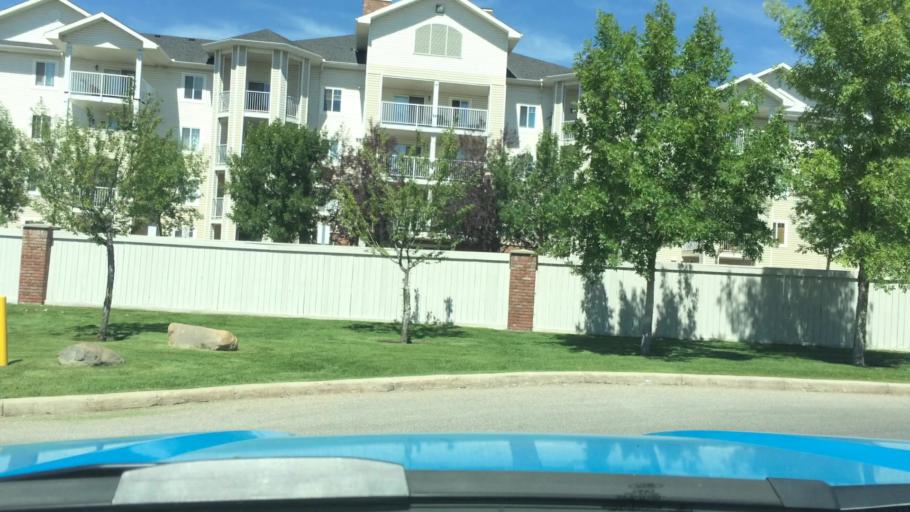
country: CA
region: Alberta
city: Calgary
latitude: 51.1555
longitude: -114.0535
